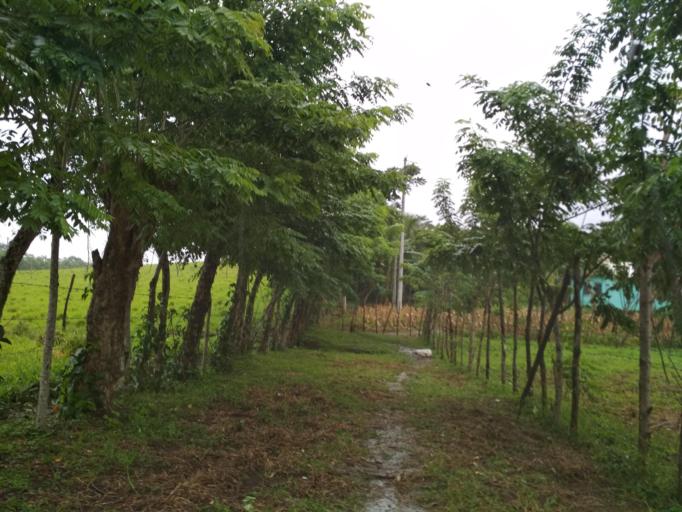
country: MX
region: Veracruz
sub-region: San Andres Tuxtla
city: Soyata
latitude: 18.4141
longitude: -95.3069
